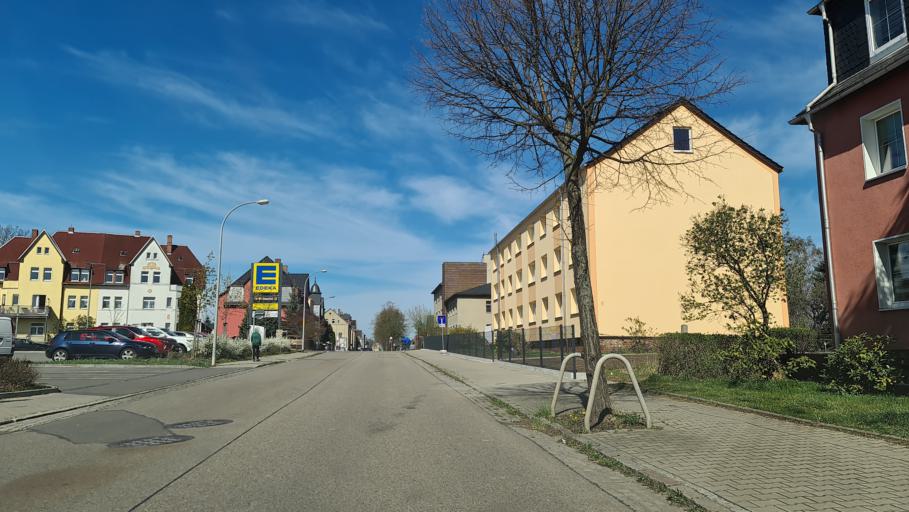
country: DE
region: Saxony
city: Burgstadt
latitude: 50.9123
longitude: 12.8095
